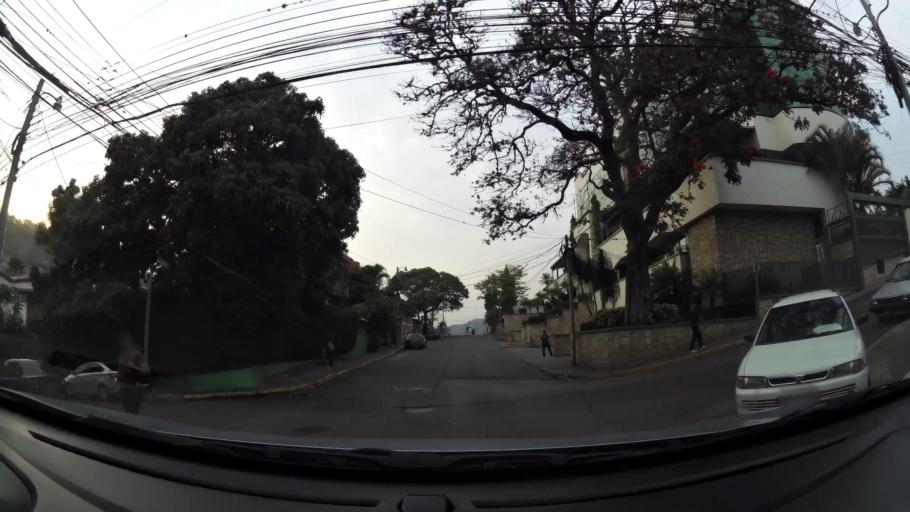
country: HN
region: Francisco Morazan
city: Tegucigalpa
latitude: 14.0922
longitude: -87.1956
